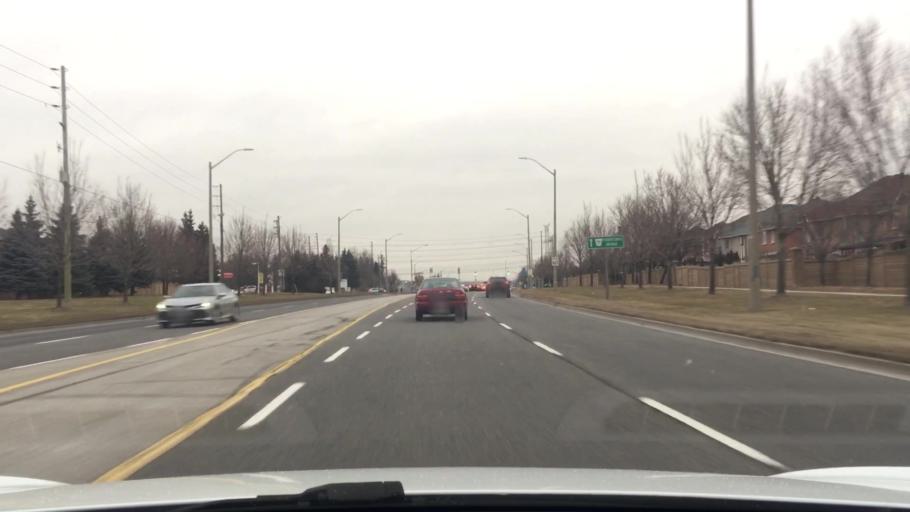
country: CA
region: Ontario
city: Markham
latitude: 43.8470
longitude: -79.2793
